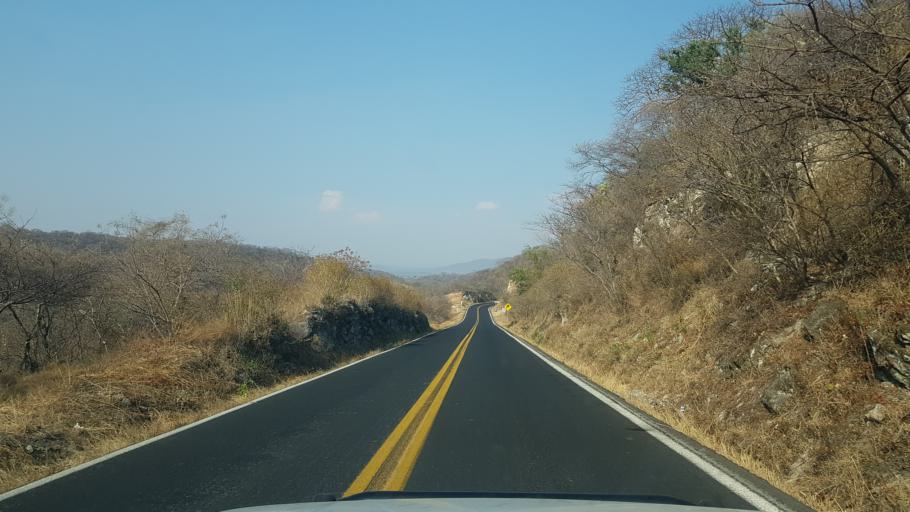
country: MX
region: Puebla
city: Calmeca
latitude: 18.6450
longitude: -98.6026
